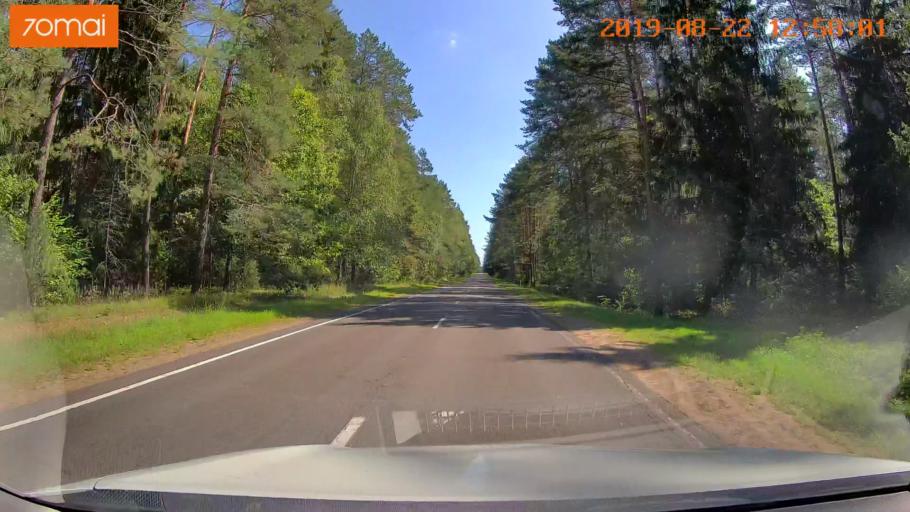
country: BY
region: Minsk
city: Prawdzinski
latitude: 53.4262
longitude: 27.7611
